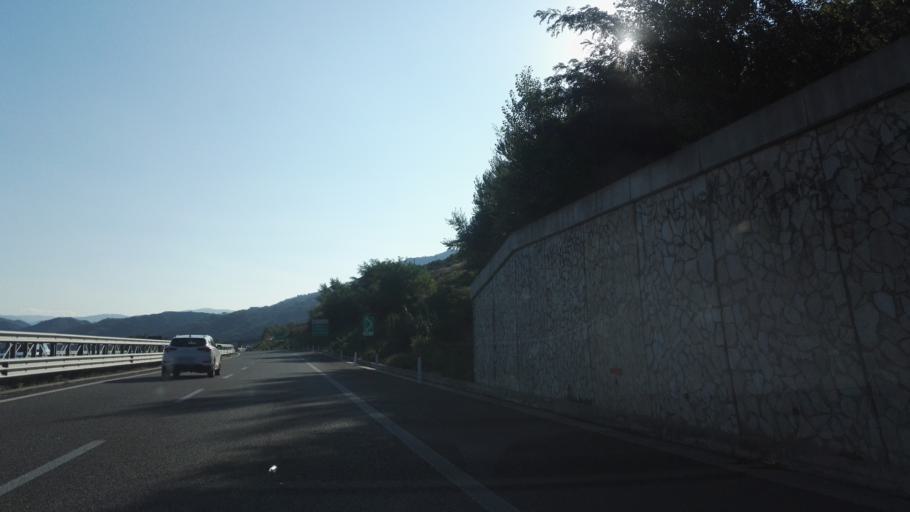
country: IT
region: Calabria
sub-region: Provincia di Catanzaro
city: Nocera Terinese
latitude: 39.0597
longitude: 16.1634
